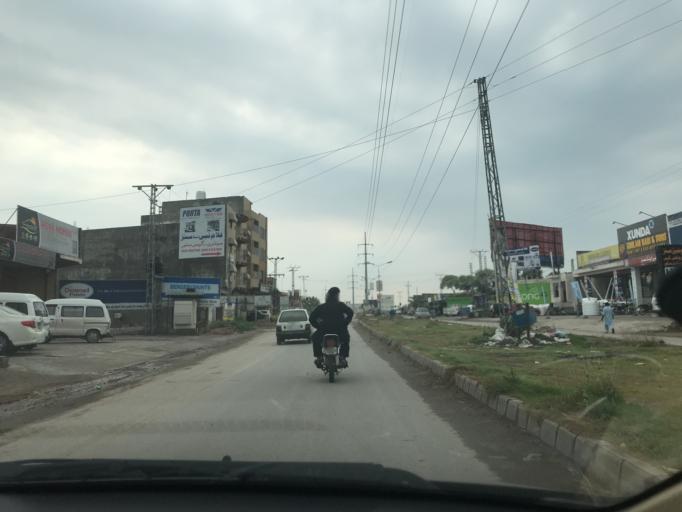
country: PK
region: Islamabad
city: Islamabad
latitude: 33.6859
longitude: 73.1638
